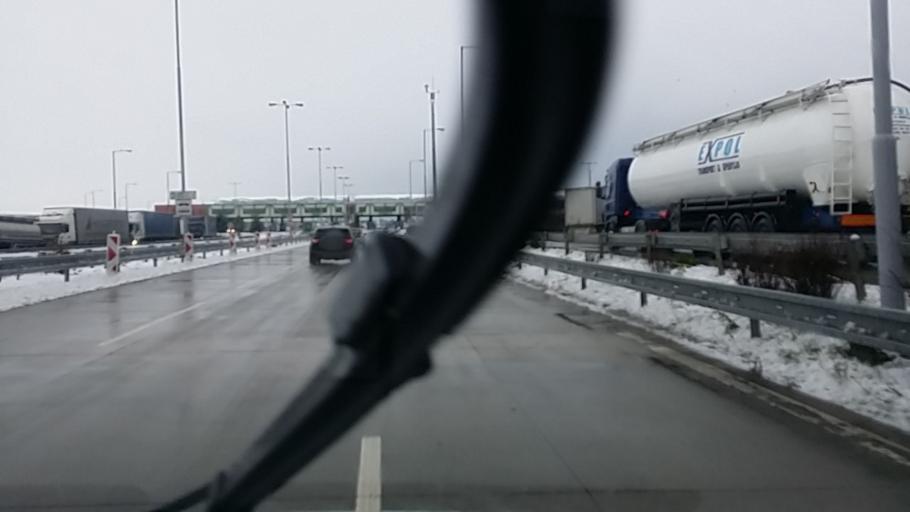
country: HU
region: Gyor-Moson-Sopron
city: Rajka
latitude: 48.0140
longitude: 17.1751
